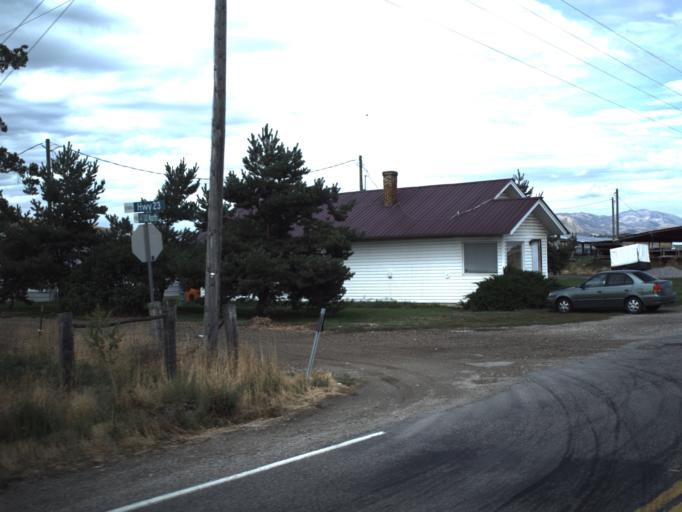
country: US
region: Utah
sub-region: Cache County
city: Lewiston
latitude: 41.9984
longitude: -111.9550
